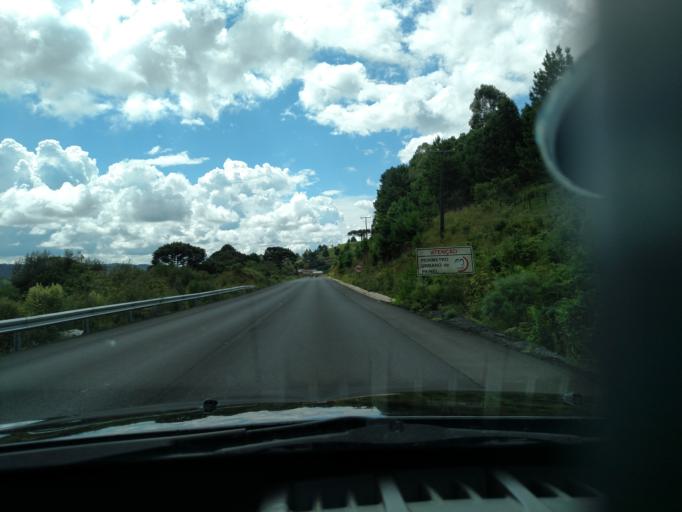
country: BR
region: Santa Catarina
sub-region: Lages
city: Lages
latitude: -27.9308
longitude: -50.0975
